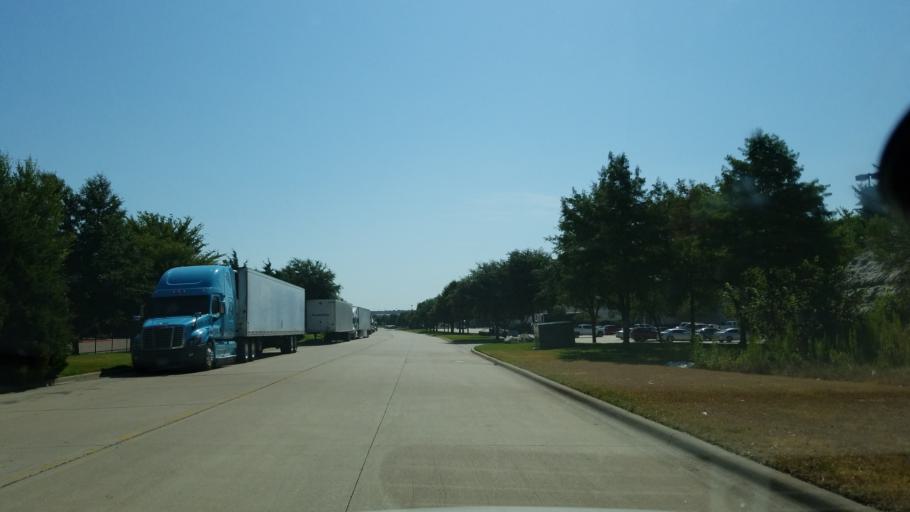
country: US
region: Texas
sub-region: Dallas County
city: Cockrell Hill
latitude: 32.7522
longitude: -96.8887
